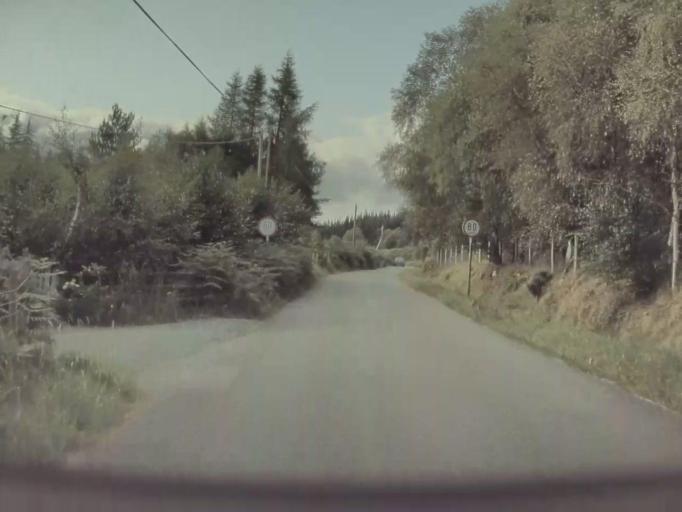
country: IE
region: Leinster
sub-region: Wicklow
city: Rathdrum
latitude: 53.0109
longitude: -6.2958
